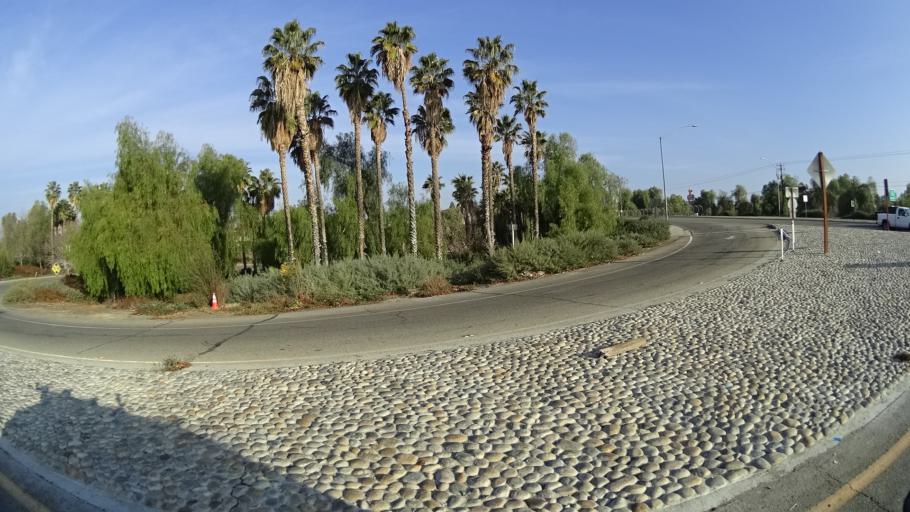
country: US
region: California
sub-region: Kern County
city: Bakersfield
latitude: 35.3952
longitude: -118.9503
